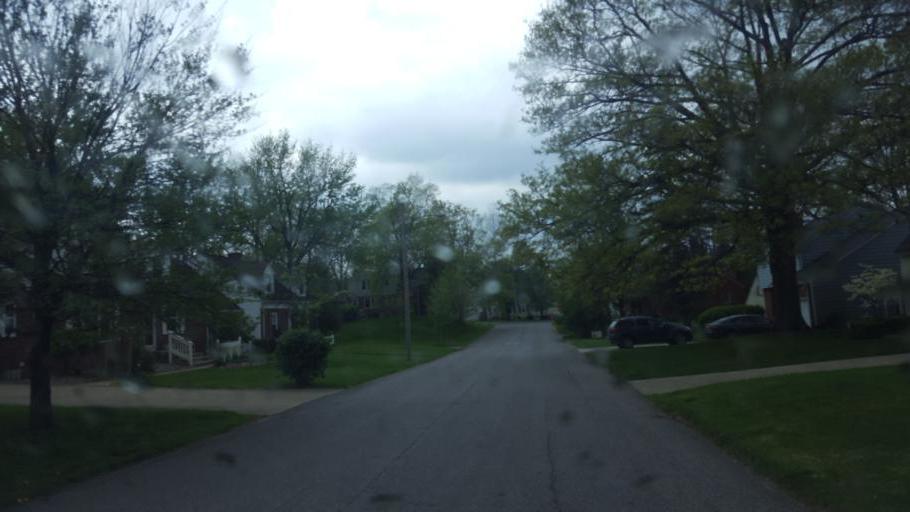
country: US
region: Ohio
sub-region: Richland County
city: Mansfield
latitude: 40.7507
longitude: -82.5414
